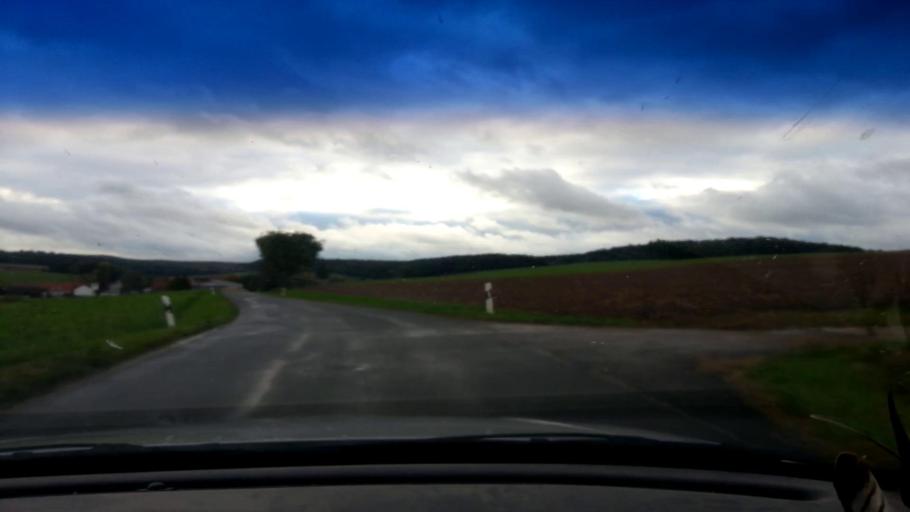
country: DE
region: Bavaria
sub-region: Upper Franconia
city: Burgwindheim
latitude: 49.8100
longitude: 10.6481
